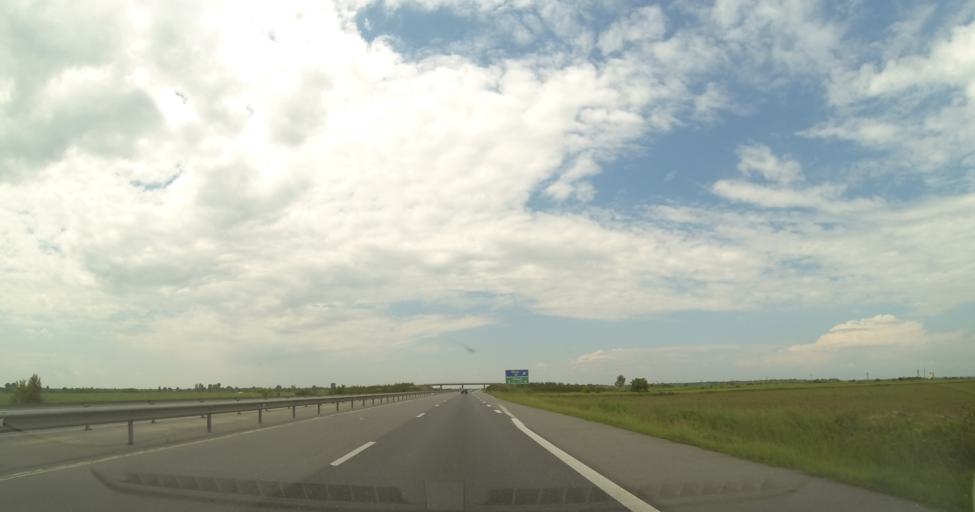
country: RO
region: Dambovita
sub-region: Comuna Mogosani
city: Zavoiu
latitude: 44.6293
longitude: 25.4180
